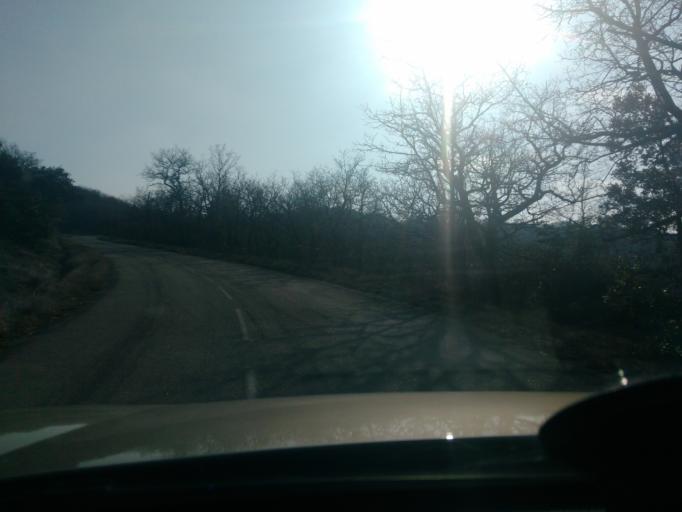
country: FR
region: Rhone-Alpes
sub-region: Departement de la Drome
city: La Begude-de-Mazenc
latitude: 44.4931
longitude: 4.8753
